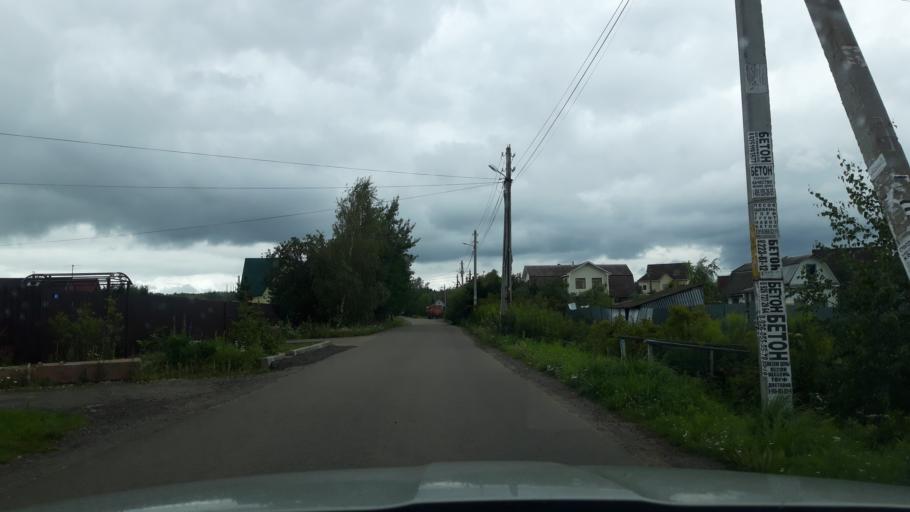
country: RU
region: Moskovskaya
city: Peshki
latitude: 56.0989
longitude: 37.0663
